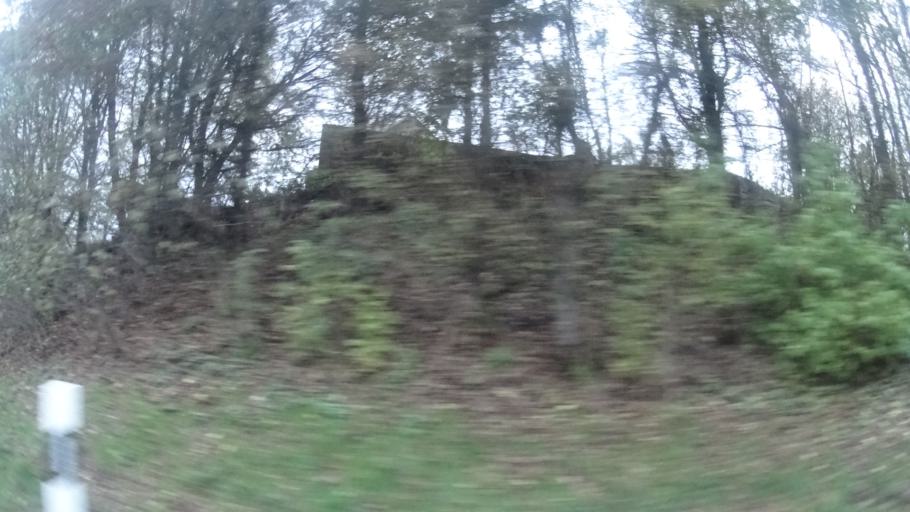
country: DE
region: Hesse
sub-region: Regierungsbezirk Giessen
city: Freiensteinau
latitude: 50.3996
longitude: 9.4247
